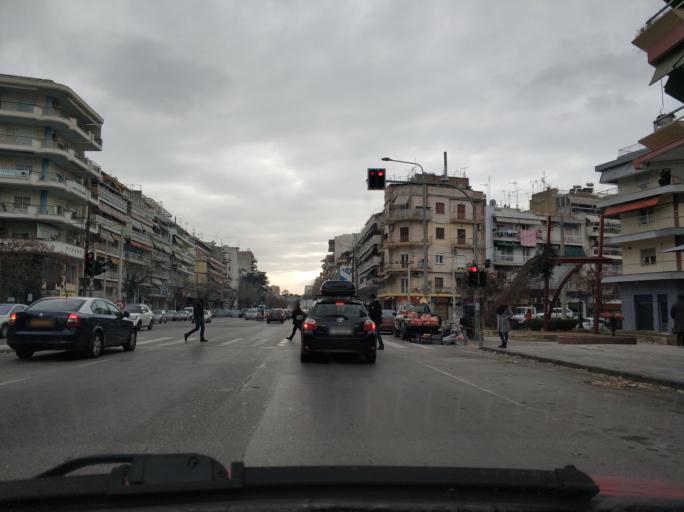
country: GR
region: Central Macedonia
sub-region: Nomos Thessalonikis
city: Triandria
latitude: 40.6026
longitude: 22.9641
